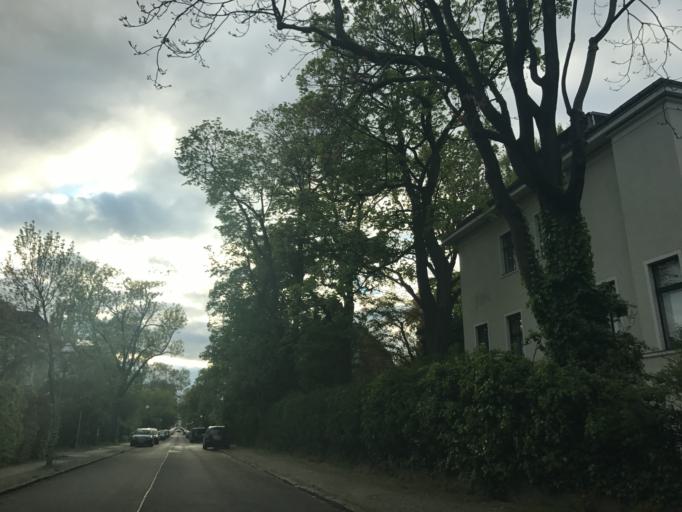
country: DE
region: Berlin
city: Westend
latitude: 52.5153
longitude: 13.2706
